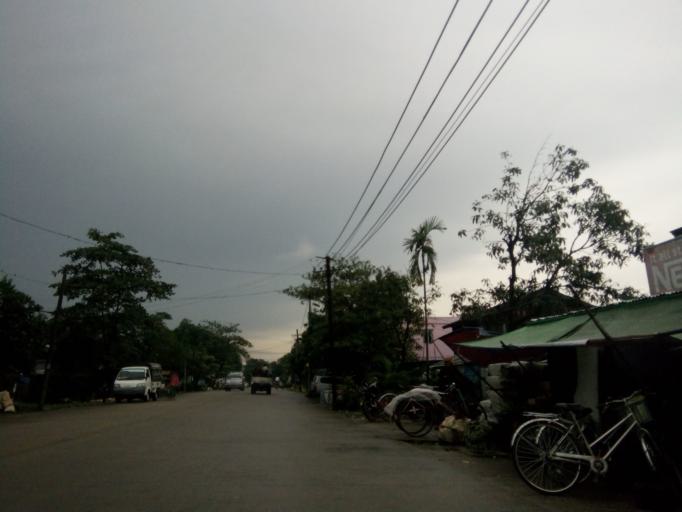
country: MM
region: Yangon
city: Yangon
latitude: 16.9157
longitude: 96.1604
